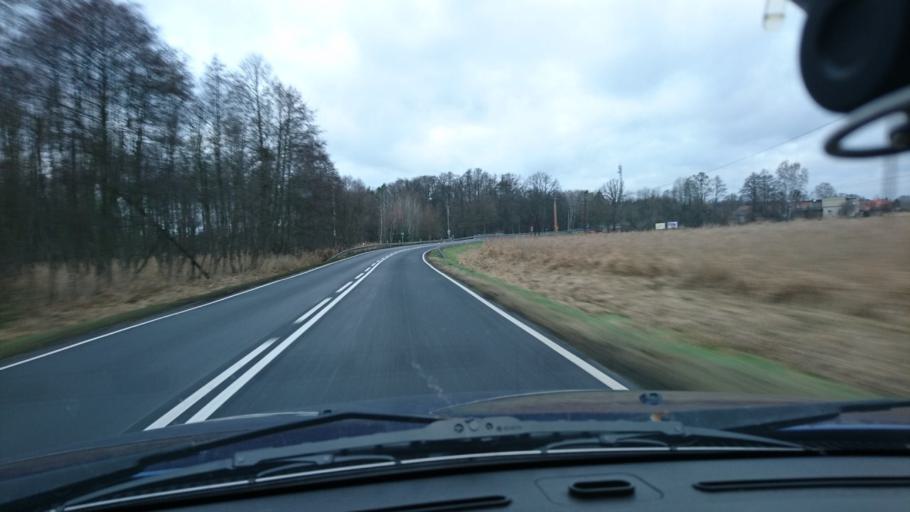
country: PL
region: Opole Voivodeship
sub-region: Powiat kluczborski
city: Kluczbork
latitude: 50.9533
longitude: 18.3098
